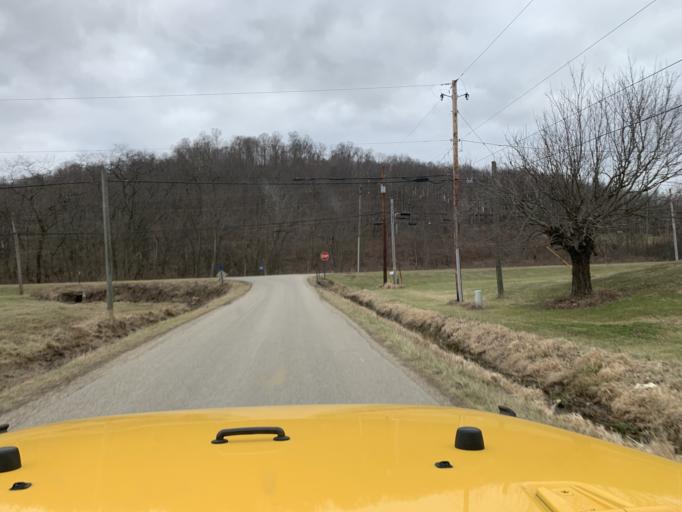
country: US
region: Ohio
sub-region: Tuscarawas County
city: Newcomerstown
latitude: 40.3008
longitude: -81.5520
